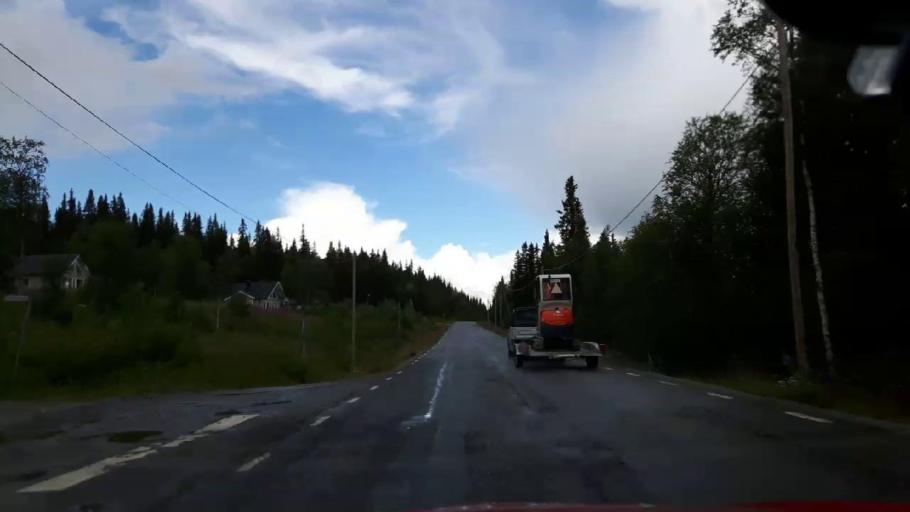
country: SE
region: Vaesterbotten
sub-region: Vilhelmina Kommun
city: Sjoberg
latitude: 64.9746
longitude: 15.3270
